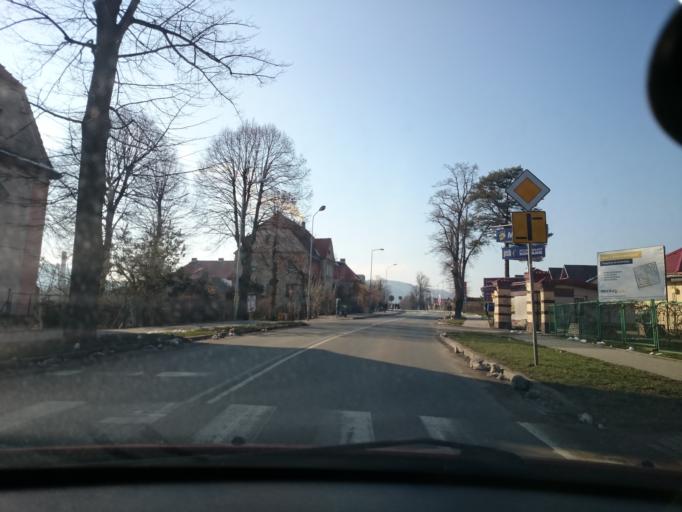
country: PL
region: Lower Silesian Voivodeship
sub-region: Powiat klodzki
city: Bystrzyca Klodzka
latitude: 50.3020
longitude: 16.6422
